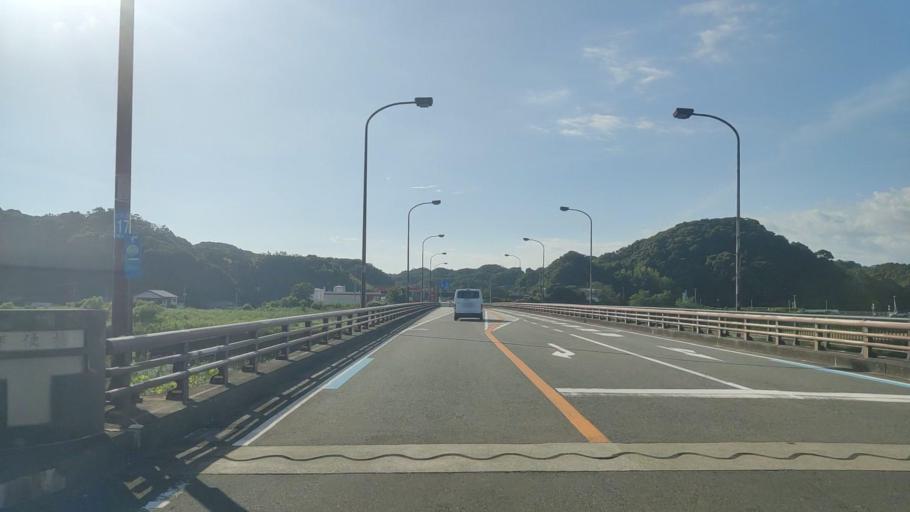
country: JP
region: Wakayama
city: Tanabe
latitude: 33.6796
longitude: 135.4090
